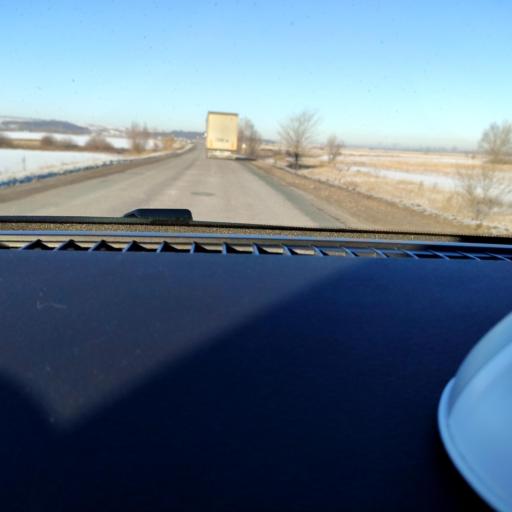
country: RU
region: Samara
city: Spiridonovka
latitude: 53.1337
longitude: 50.6103
